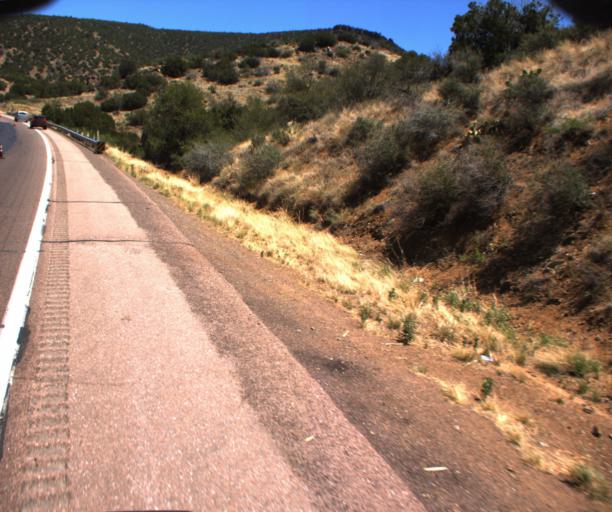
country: US
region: Arizona
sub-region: Gila County
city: Payson
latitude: 34.1498
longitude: -111.3159
